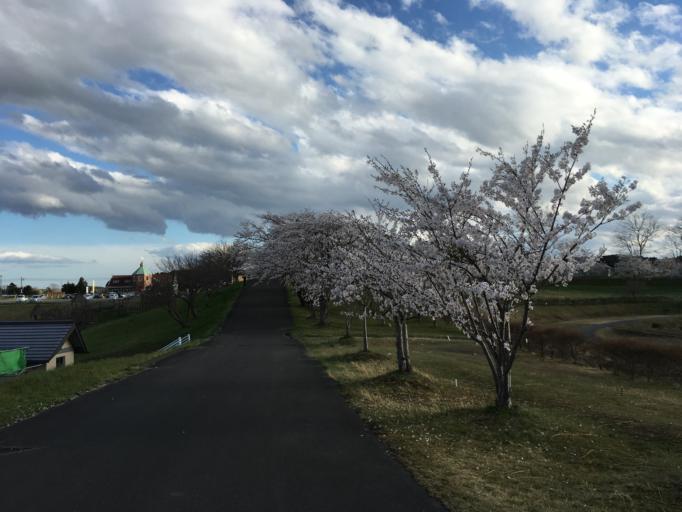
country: JP
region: Miyagi
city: Wakuya
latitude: 38.6906
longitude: 141.1340
